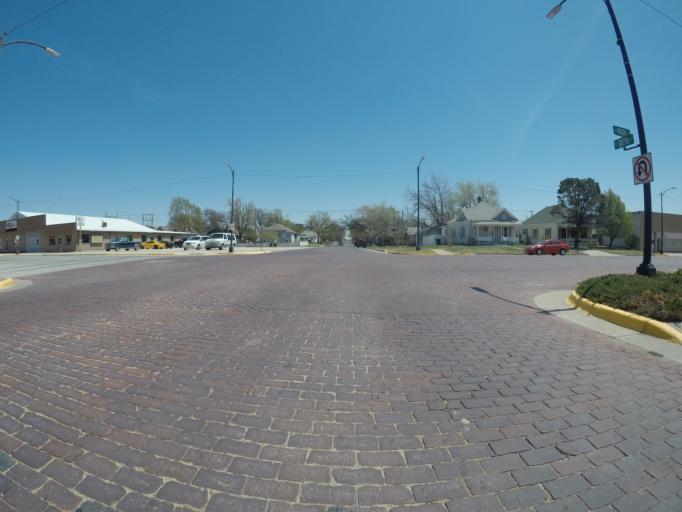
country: US
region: Kansas
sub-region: Pratt County
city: Pratt
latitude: 37.6408
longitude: -98.7397
